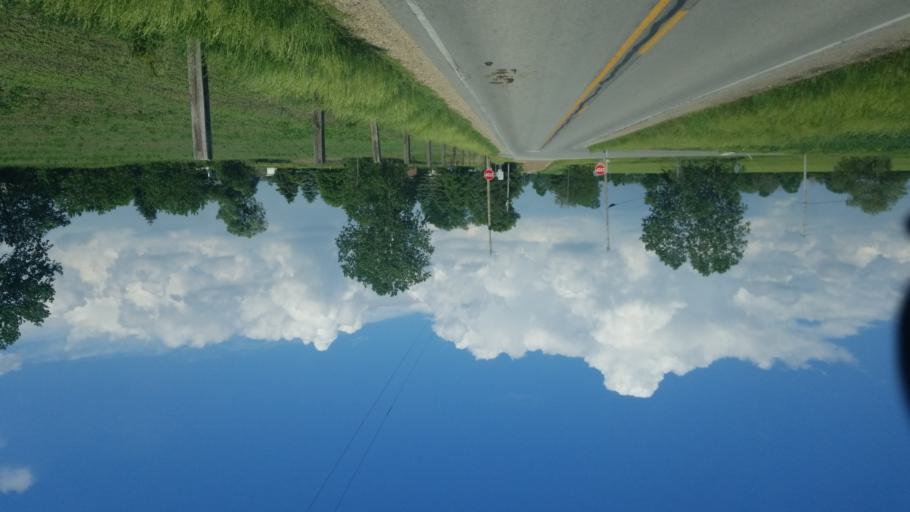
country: US
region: Indiana
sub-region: Marshall County
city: Bourbon
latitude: 41.3144
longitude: -86.0394
